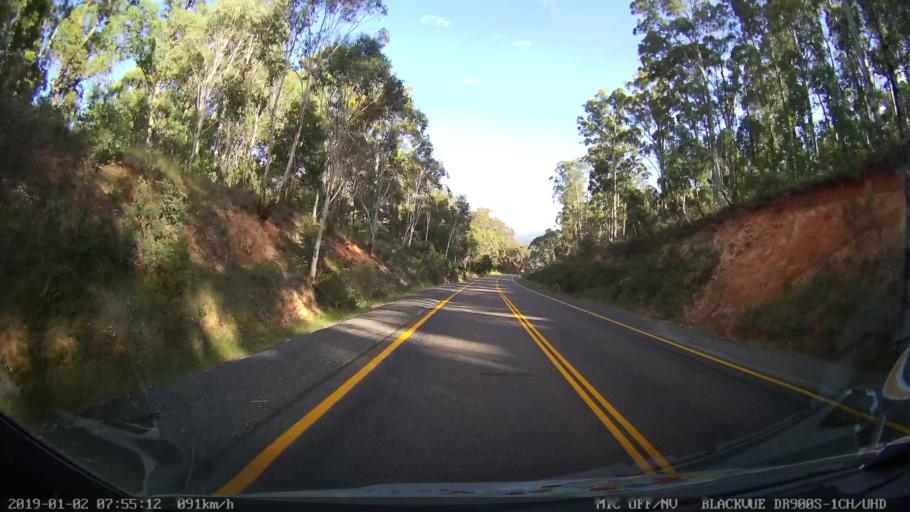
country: AU
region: New South Wales
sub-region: Tumut Shire
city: Tumut
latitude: -35.6881
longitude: 148.4886
